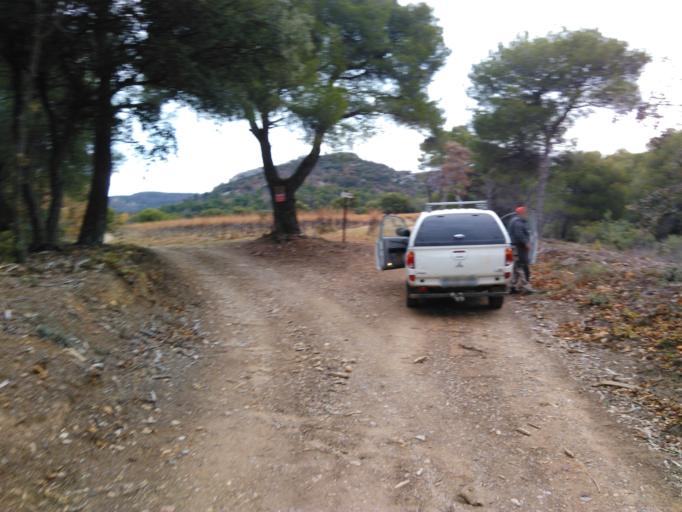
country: FR
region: Rhone-Alpes
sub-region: Departement de la Drome
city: Mirabel-aux-Baronnies
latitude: 44.2938
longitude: 5.1459
